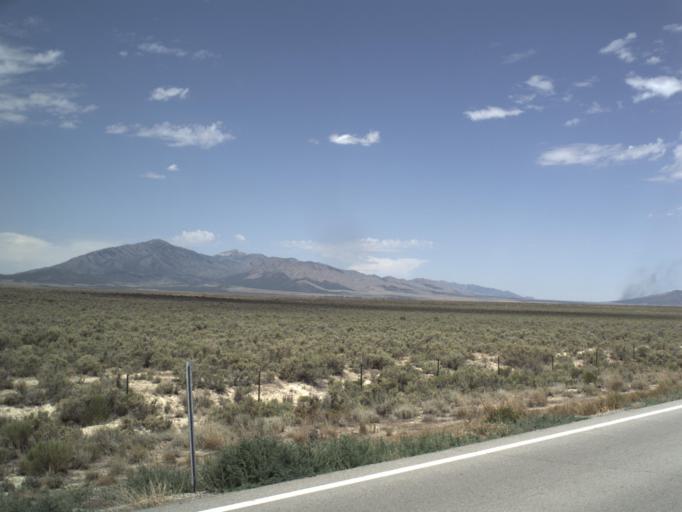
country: US
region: Utah
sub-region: Tooele County
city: Tooele
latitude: 40.2271
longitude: -112.4040
